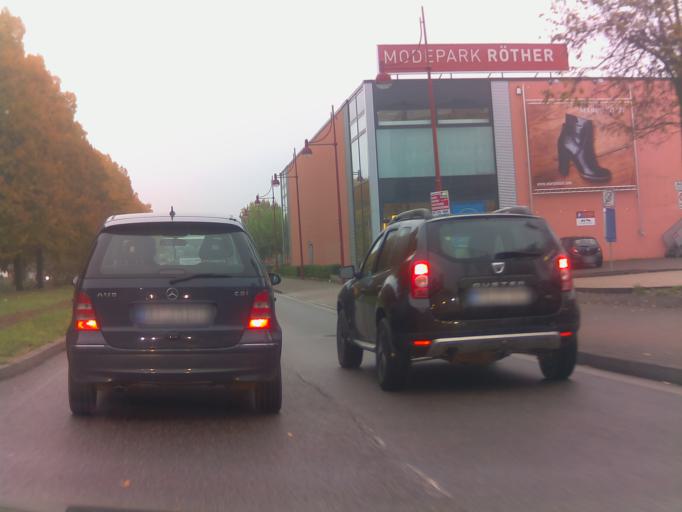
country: DE
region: Baden-Wuerttemberg
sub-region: Karlsruhe Region
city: Bretten
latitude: 49.0356
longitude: 8.7019
